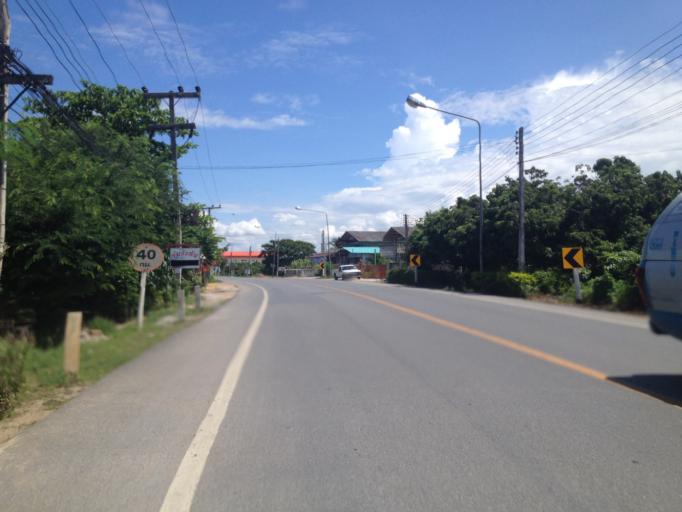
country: TH
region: Lamphun
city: Lamphun
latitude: 18.6135
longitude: 98.9571
